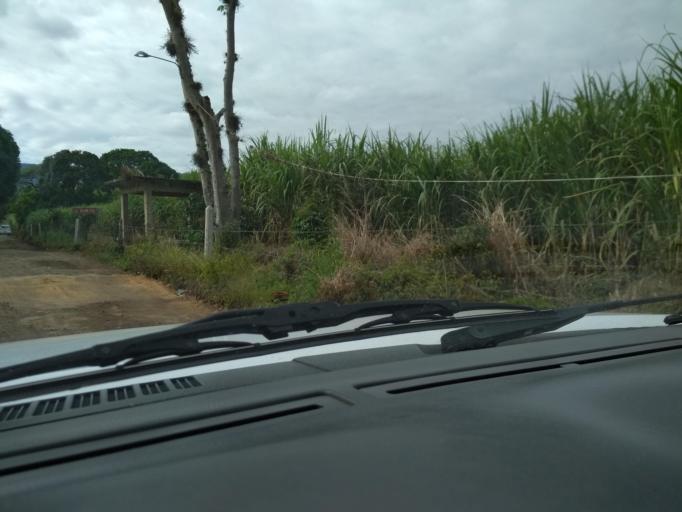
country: MX
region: Veracruz
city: Alto Lucero
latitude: 19.5887
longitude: -96.7838
